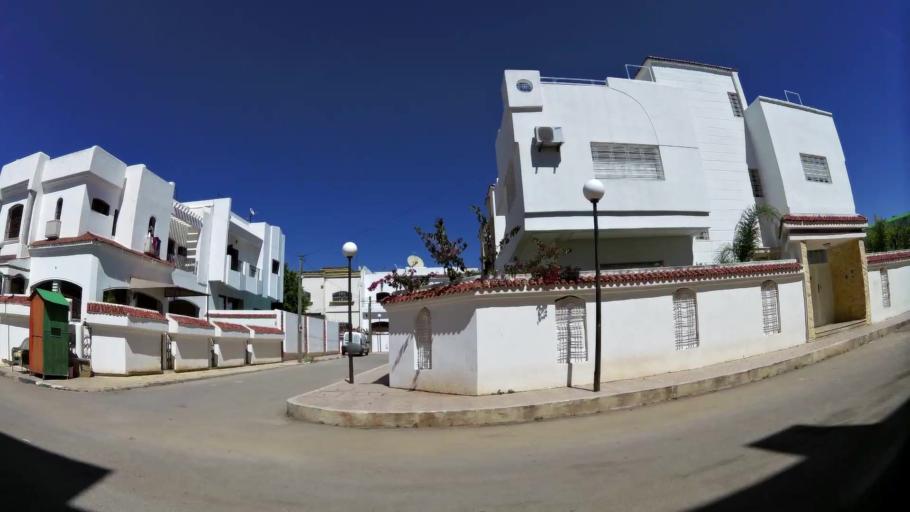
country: MA
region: Fes-Boulemane
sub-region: Fes
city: Fes
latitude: 34.0151
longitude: -5.0008
